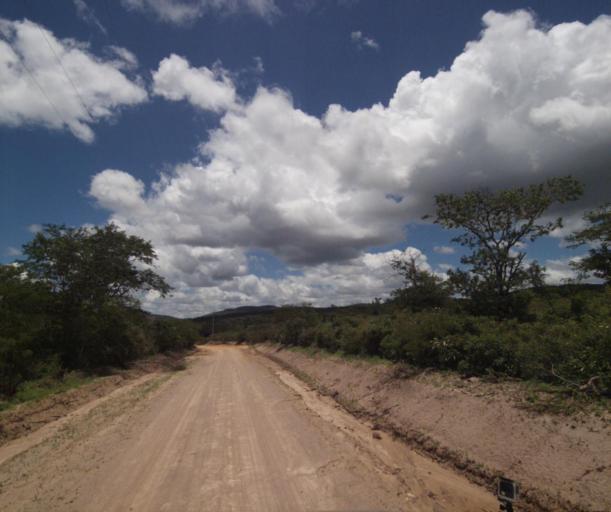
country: BR
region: Bahia
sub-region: Pocoes
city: Pocoes
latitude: -14.3813
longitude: -40.3869
